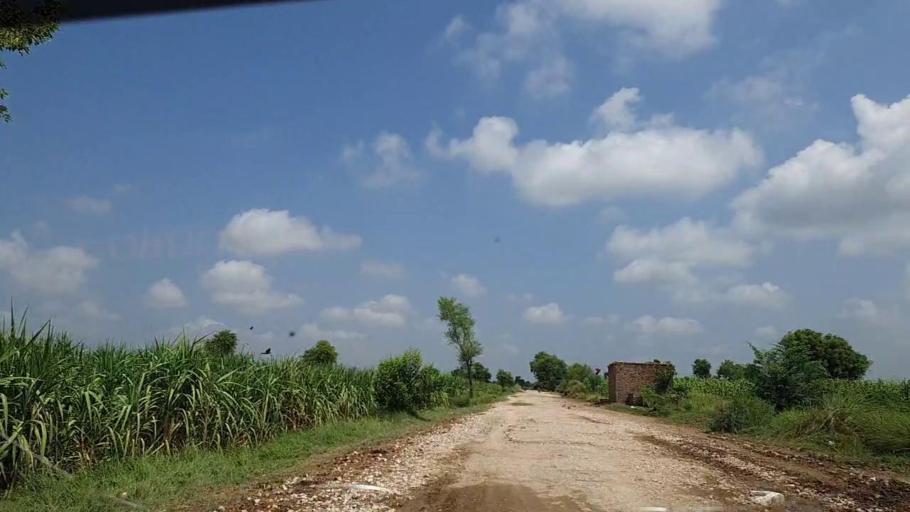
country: PK
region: Sindh
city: Tharu Shah
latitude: 26.9006
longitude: 68.0393
